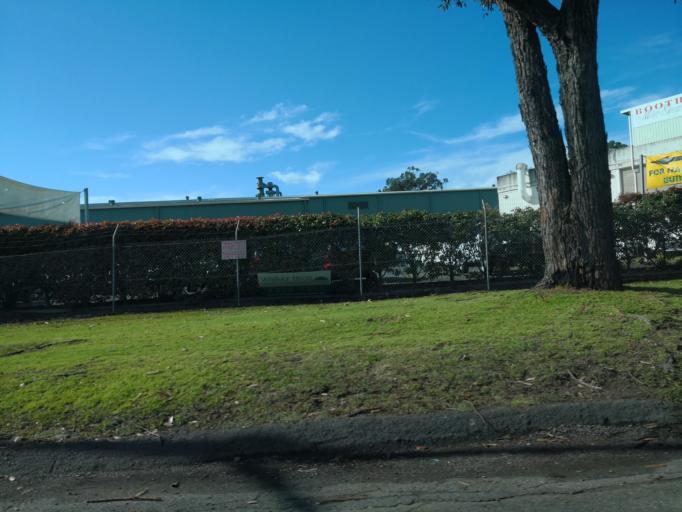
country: AU
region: New South Wales
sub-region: Gosford Shire
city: Narara
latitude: -33.4116
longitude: 151.3459
